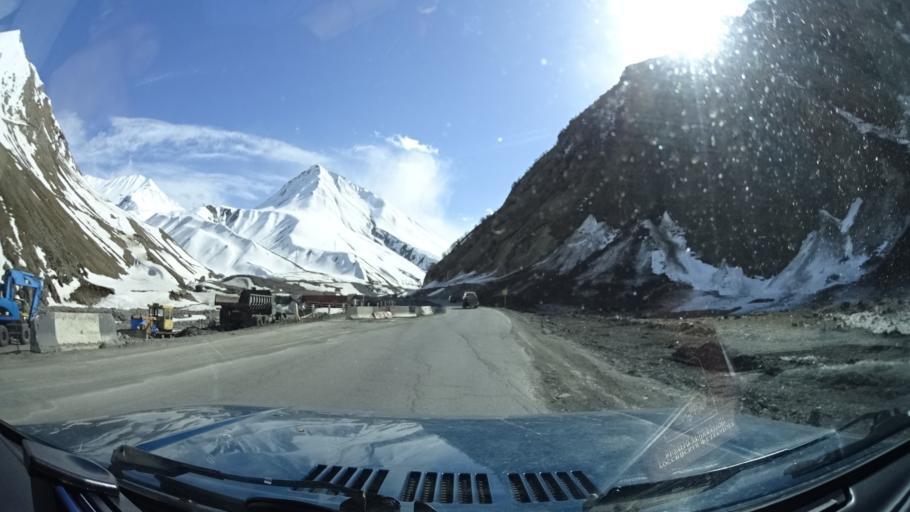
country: GE
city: Gudauri
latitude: 42.5476
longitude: 44.4923
